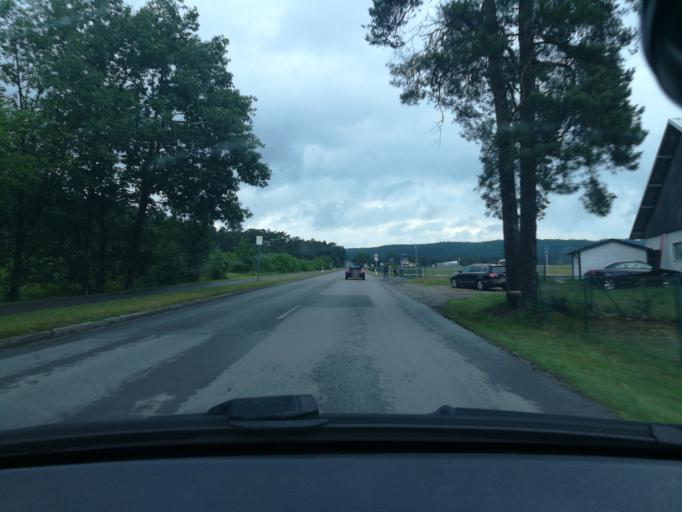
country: DE
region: North Rhine-Westphalia
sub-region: Regierungsbezirk Detmold
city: Oerlinghausen
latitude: 51.9273
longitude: 8.6569
